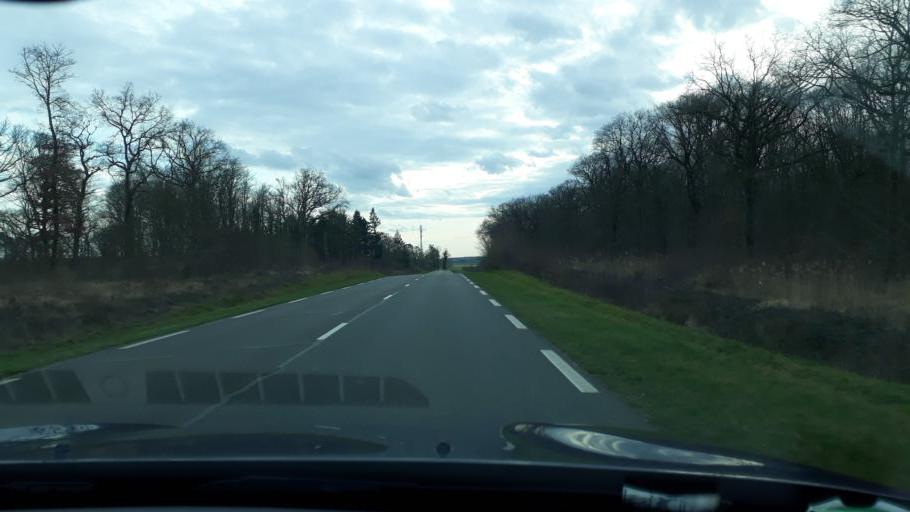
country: FR
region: Centre
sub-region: Departement du Loiret
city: Loury
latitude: 48.0234
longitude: 2.1155
